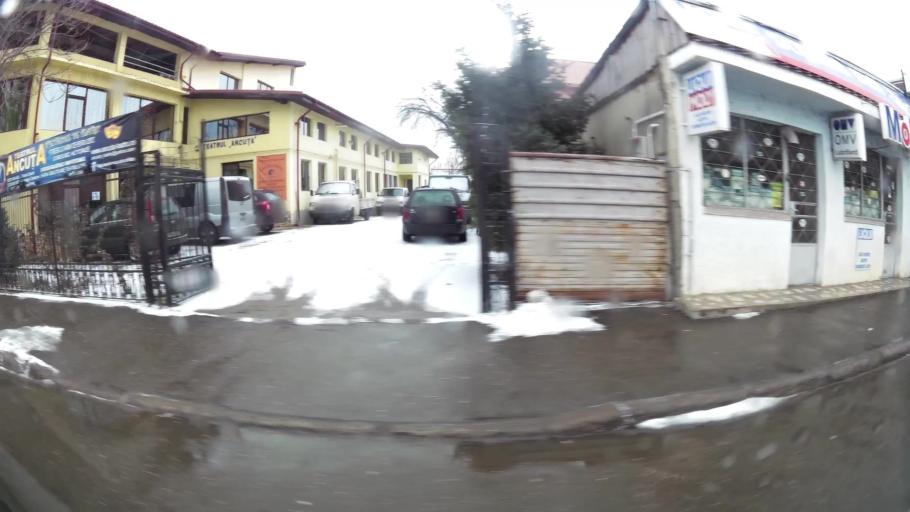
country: RO
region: Prahova
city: Ploiesti
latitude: 44.9482
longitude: 26.0242
